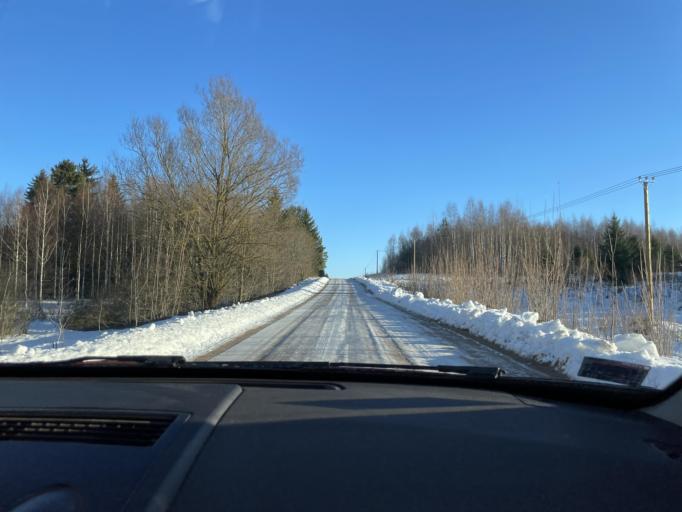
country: LV
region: Ludzas Rajons
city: Ludza
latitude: 56.4605
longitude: 27.6173
